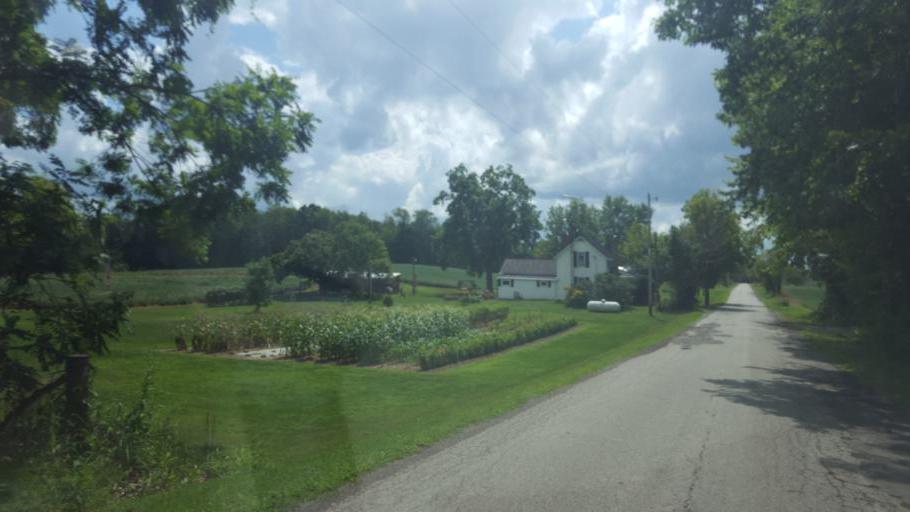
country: US
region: Ohio
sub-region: Morrow County
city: Mount Gilead
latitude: 40.4362
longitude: -82.7471
